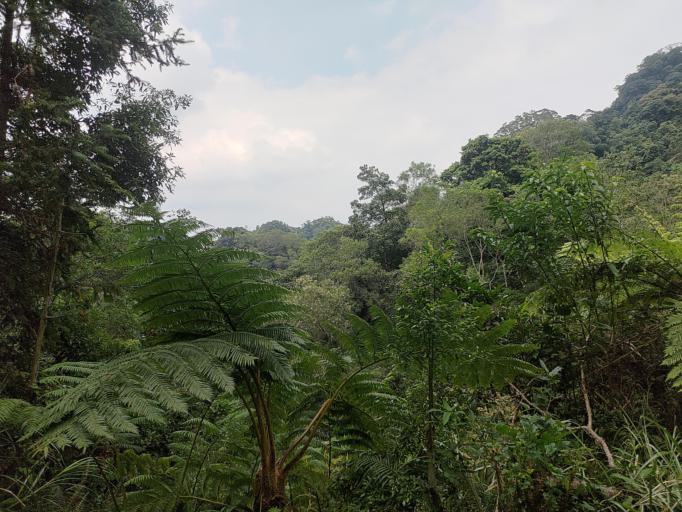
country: TW
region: Taiwan
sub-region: Hsinchu
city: Hsinchu
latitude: 24.6321
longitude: 121.0699
